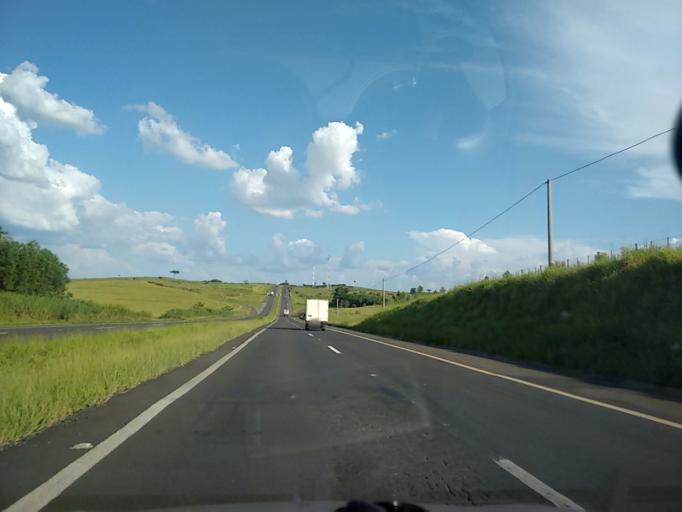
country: BR
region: Sao Paulo
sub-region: Duartina
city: Duartina
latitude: -22.2773
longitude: -49.4999
